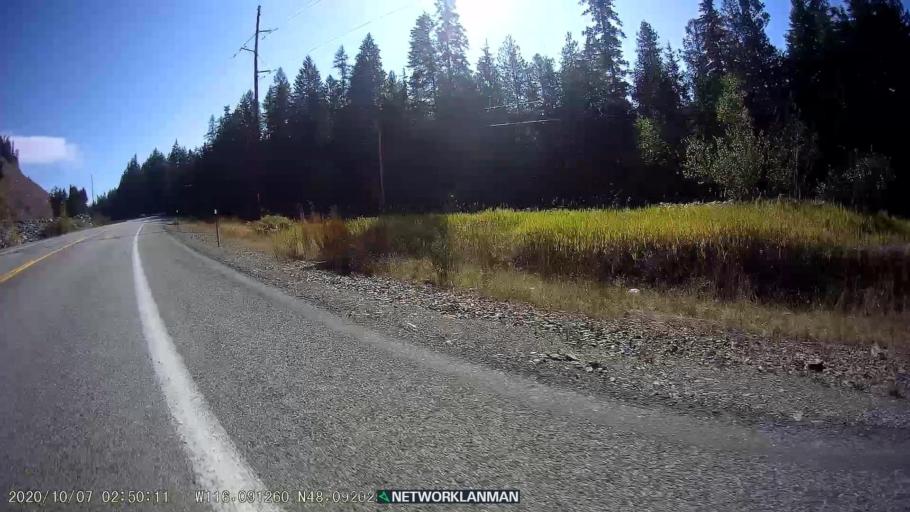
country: US
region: Idaho
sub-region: Bonner County
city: Ponderay
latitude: 48.0906
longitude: -116.0896
